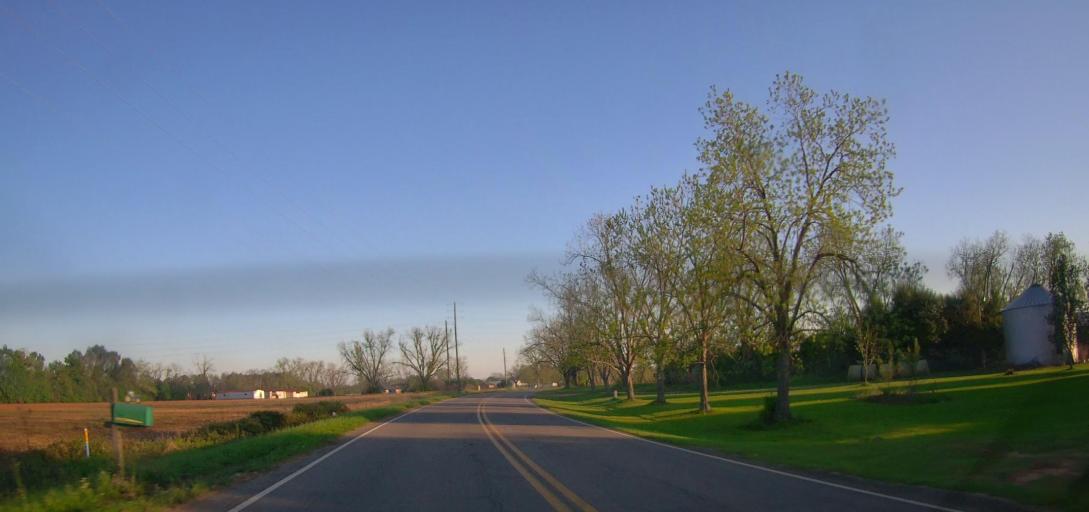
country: US
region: Georgia
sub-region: Irwin County
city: Ocilla
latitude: 31.6073
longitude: -83.2591
